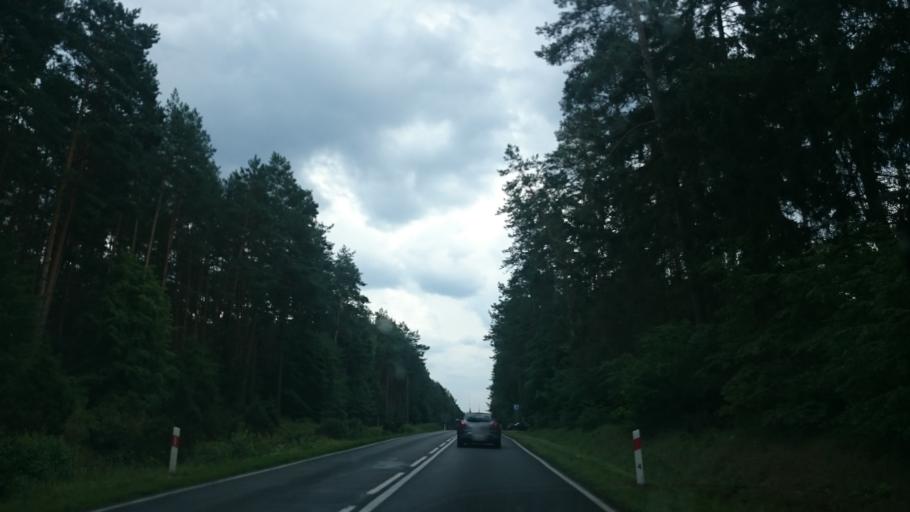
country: PL
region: Kujawsko-Pomorskie
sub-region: Powiat tucholski
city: Tuchola
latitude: 53.5485
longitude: 17.9270
